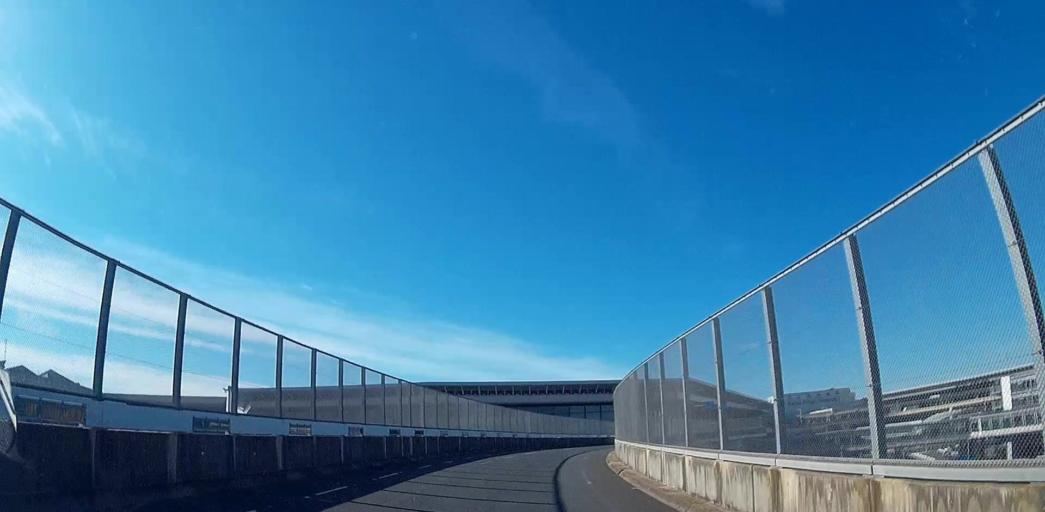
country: JP
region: Chiba
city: Narita
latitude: 35.7641
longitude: 140.3885
